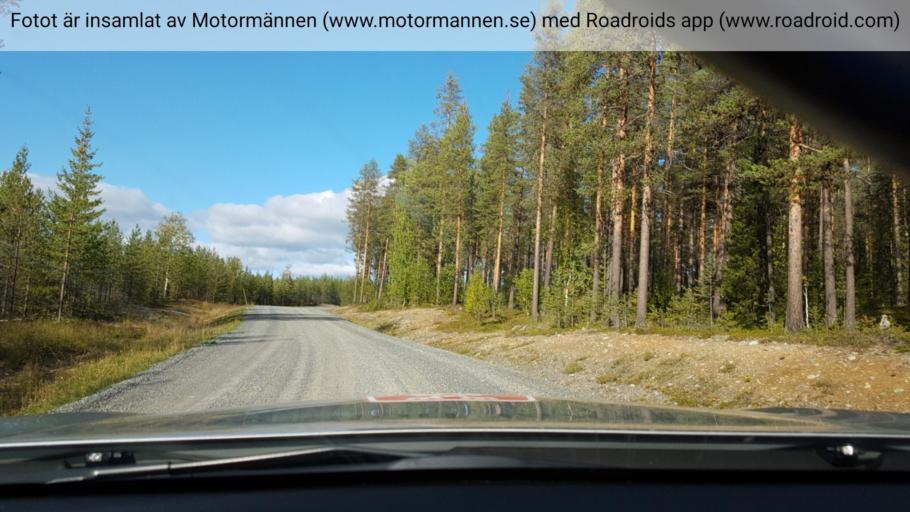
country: SE
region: Vaesterbotten
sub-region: Sorsele Kommun
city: Sorsele
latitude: 65.4505
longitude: 18.1298
